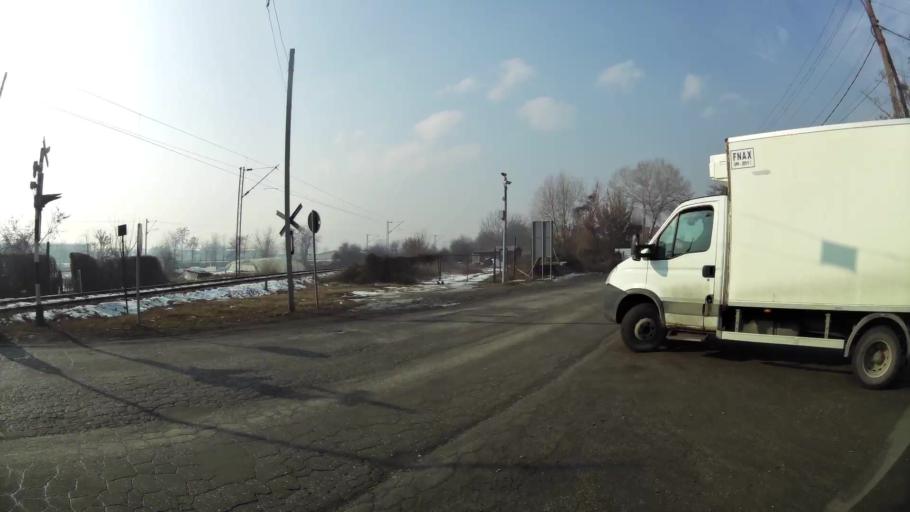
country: MK
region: Kisela Voda
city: Kisela Voda
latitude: 41.9912
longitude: 21.5100
